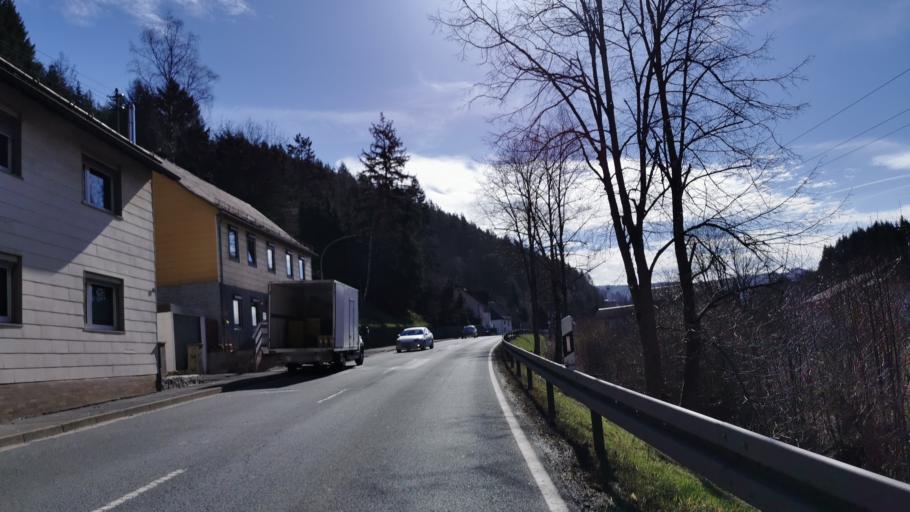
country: DE
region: Bavaria
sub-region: Upper Franconia
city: Ludwigsstadt
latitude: 50.4967
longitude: 11.3747
